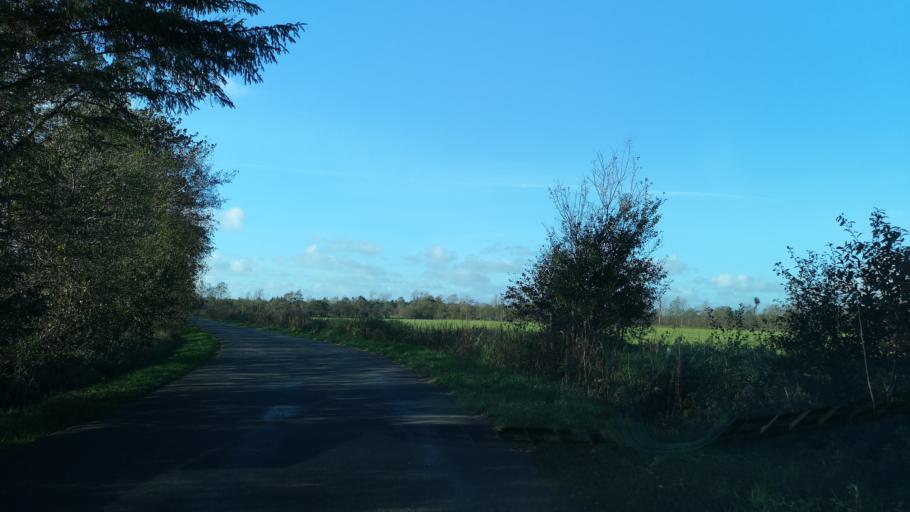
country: DK
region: Central Jutland
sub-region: Ringkobing-Skjern Kommune
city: Tarm
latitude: 55.8246
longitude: 8.4014
